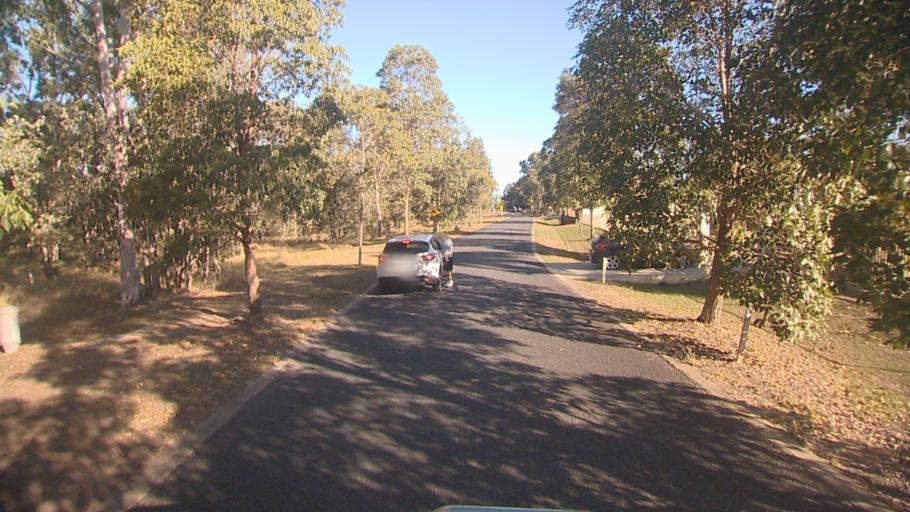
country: AU
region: Queensland
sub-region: Logan
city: North Maclean
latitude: -27.7344
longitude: 152.9709
